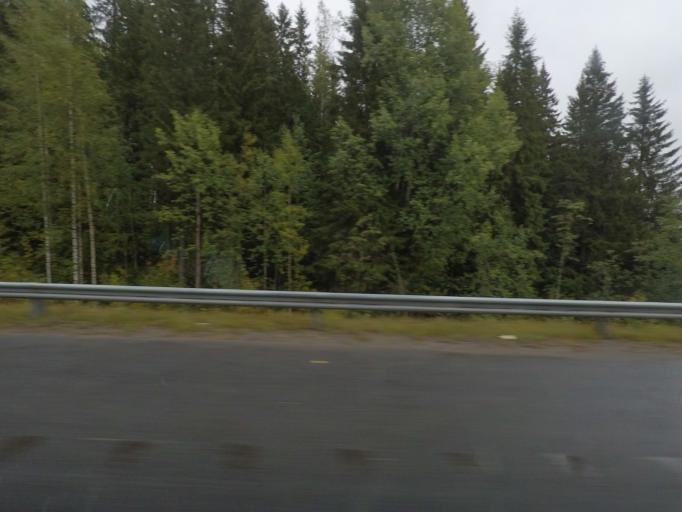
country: FI
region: Northern Savo
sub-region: Kuopio
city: Kuopio
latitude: 62.8525
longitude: 27.6213
